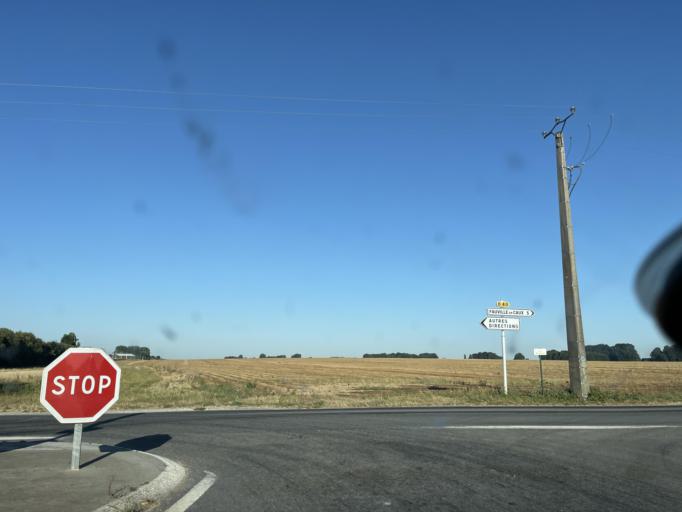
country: FR
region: Haute-Normandie
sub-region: Departement de la Seine-Maritime
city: Fauville-en-Caux
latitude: 49.6085
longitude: 0.5933
